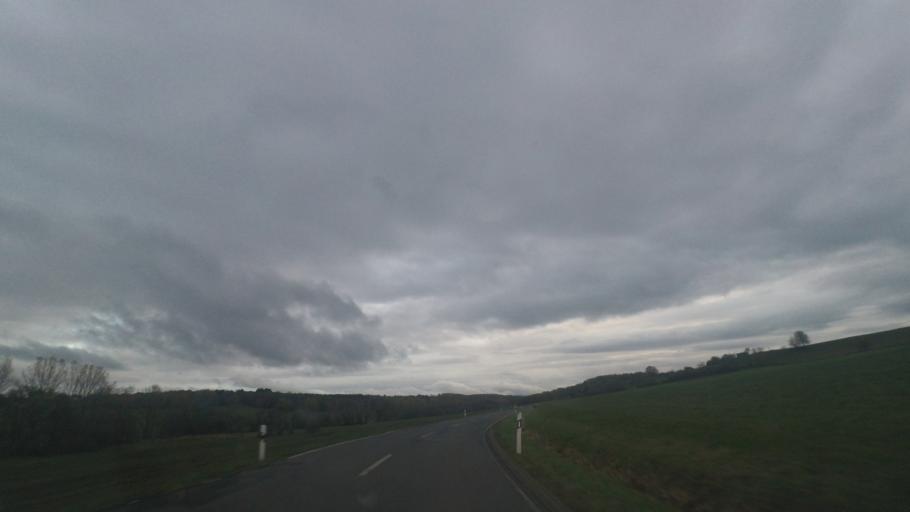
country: DE
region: Hesse
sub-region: Regierungsbezirk Darmstadt
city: Steinau an der Strasse
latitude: 50.3562
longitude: 9.4281
